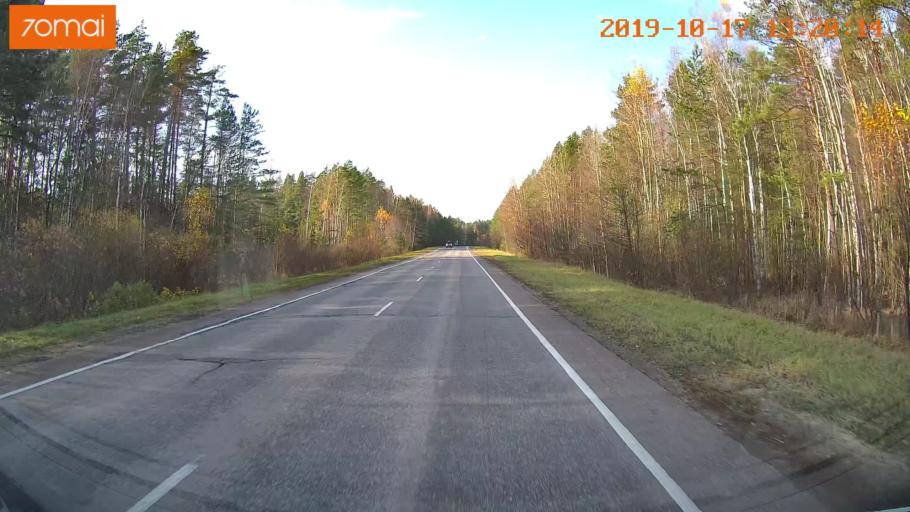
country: RU
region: Rjazan
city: Gus'-Zheleznyy
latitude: 55.0745
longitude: 41.0551
